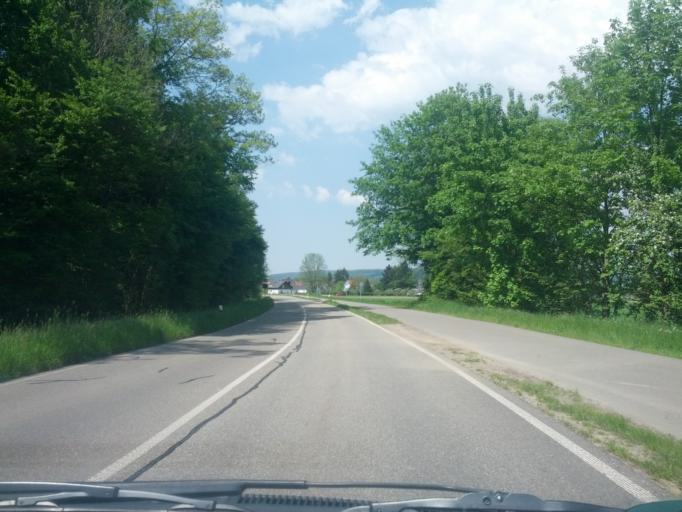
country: DE
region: Baden-Wuerttemberg
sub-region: Freiburg Region
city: Vorstetten
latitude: 48.0904
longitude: 7.8638
